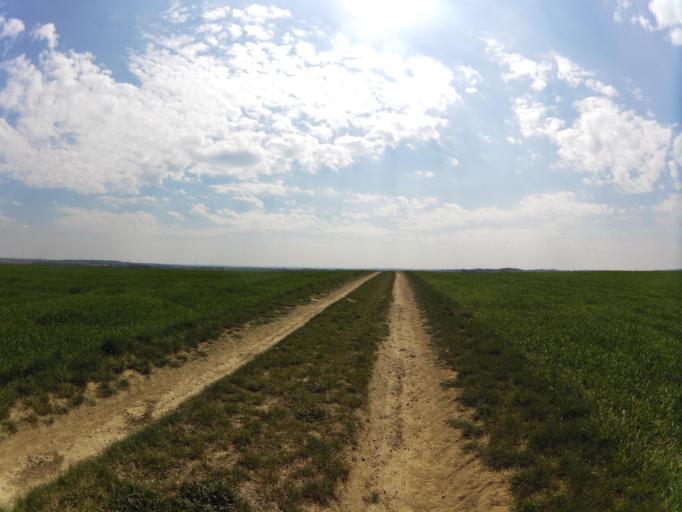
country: DE
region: Bavaria
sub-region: Regierungsbezirk Unterfranken
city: Winterhausen
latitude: 49.6819
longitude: 10.0091
